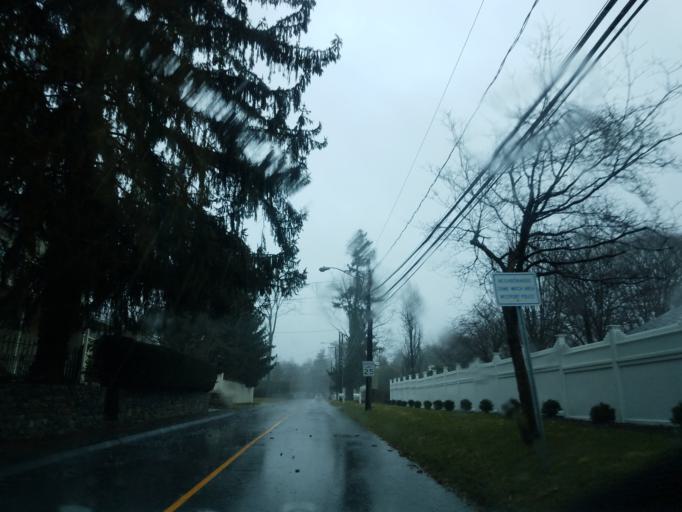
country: US
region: Connecticut
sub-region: Fairfield County
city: Westport
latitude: 41.1437
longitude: -73.3584
